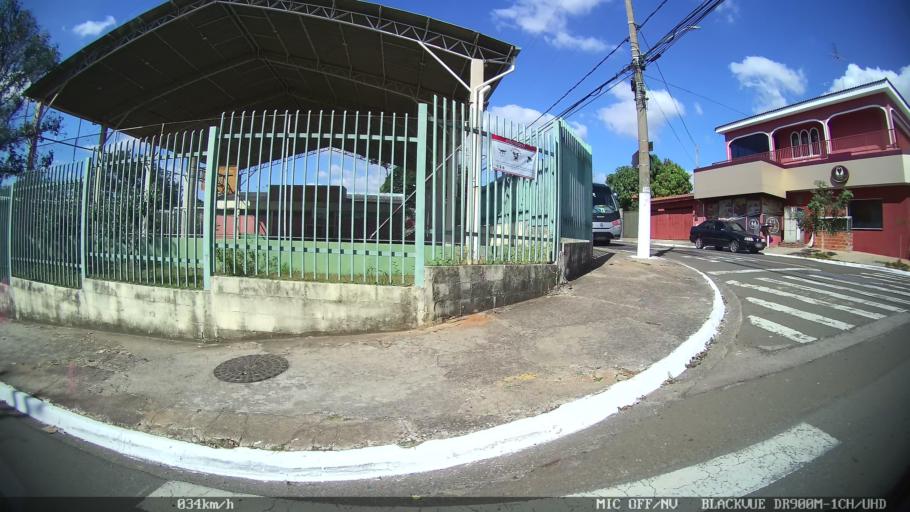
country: BR
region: Sao Paulo
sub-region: Hortolandia
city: Hortolandia
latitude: -22.8927
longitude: -47.1986
